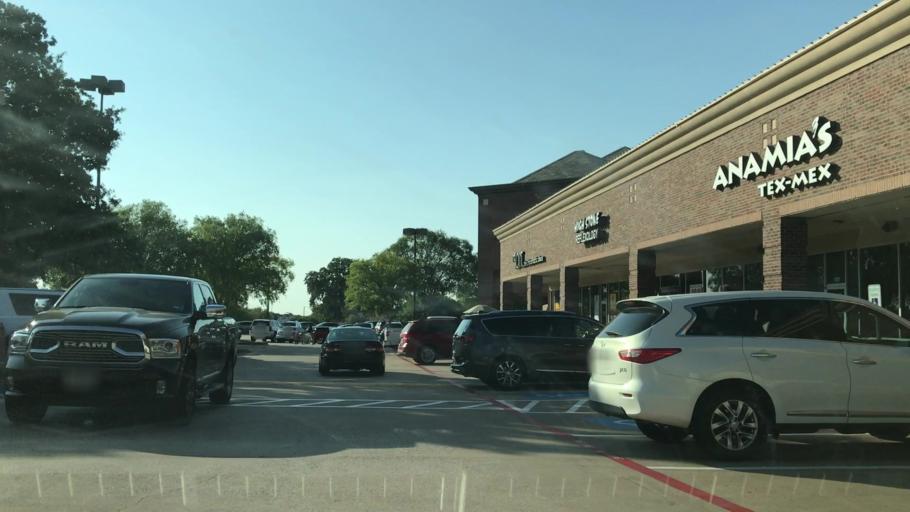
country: US
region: Texas
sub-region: Dallas County
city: Coppell
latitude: 32.9698
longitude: -96.9919
